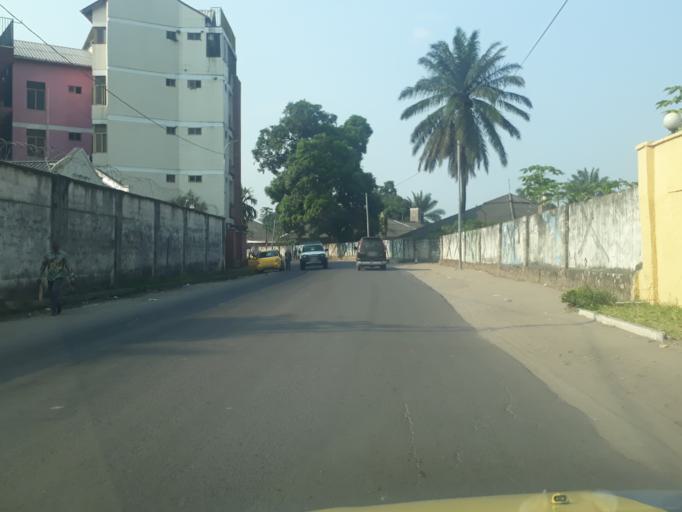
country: CD
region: Kinshasa
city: Kinshasa
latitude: -4.3156
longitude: 15.3310
